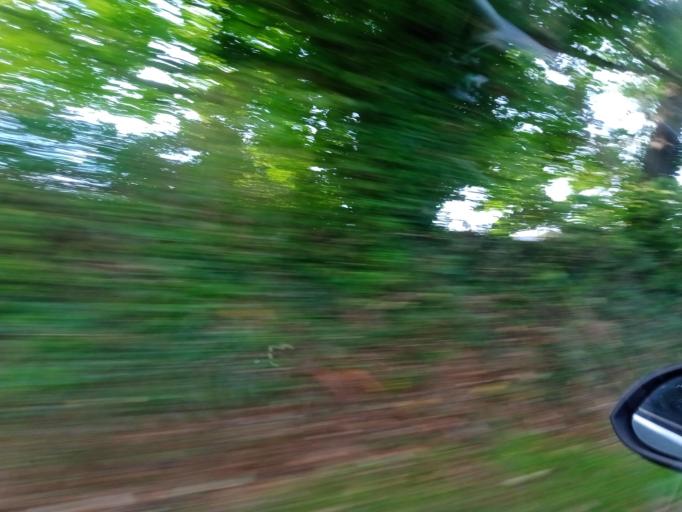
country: IE
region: Leinster
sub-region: Laois
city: Stradbally
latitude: 53.0033
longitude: -7.2126
